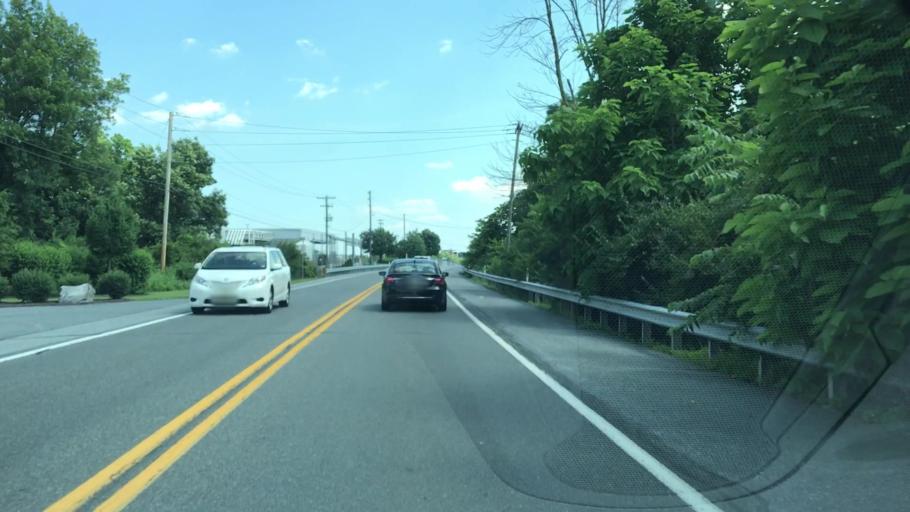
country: US
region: Pennsylvania
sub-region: Dauphin County
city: Highspire
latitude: 40.2219
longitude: -76.7926
